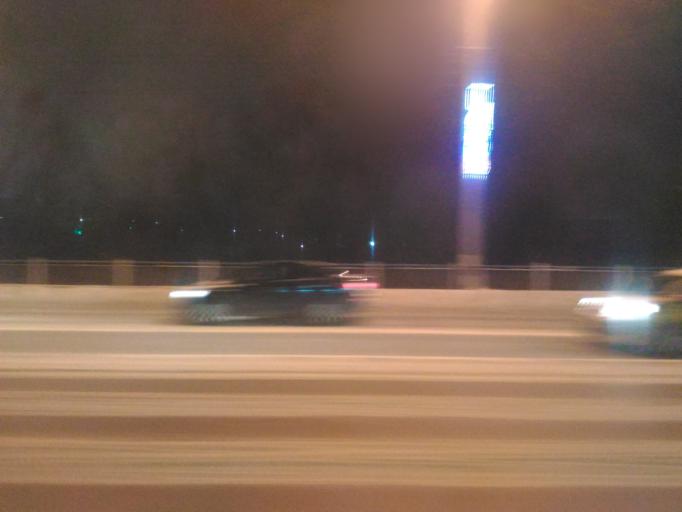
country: RU
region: Ulyanovsk
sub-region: Ulyanovskiy Rayon
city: Ulyanovsk
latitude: 54.3239
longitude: 48.3570
